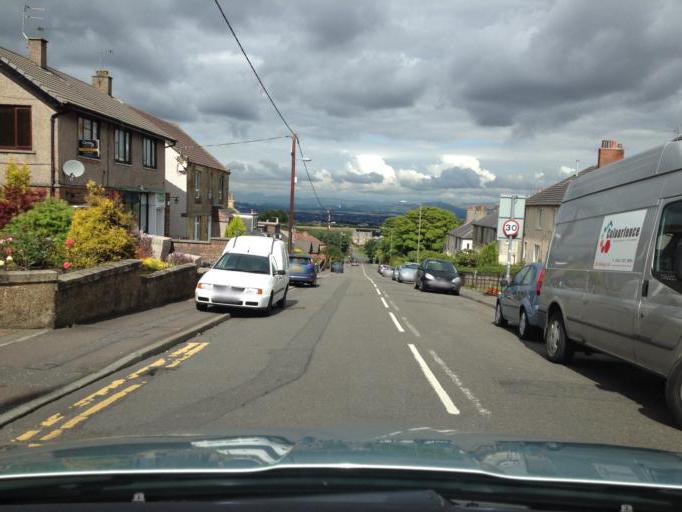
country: GB
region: Scotland
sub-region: Falkirk
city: Falkirk
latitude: 55.9712
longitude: -3.7701
